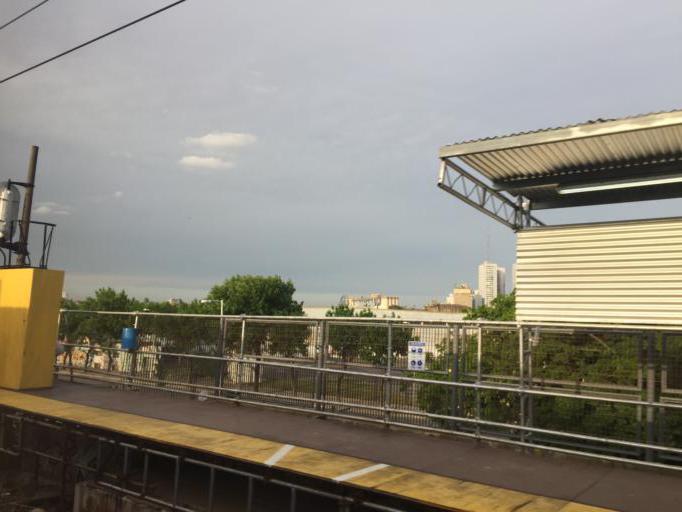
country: AR
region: Buenos Aires
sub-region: Partido de Avellaneda
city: Avellaneda
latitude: -34.6604
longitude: -58.3769
